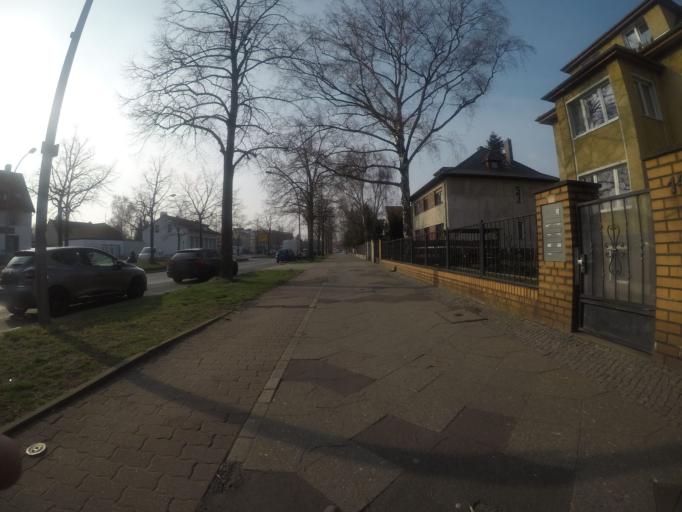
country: DE
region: Berlin
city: Gropiusstadt
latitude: 52.4335
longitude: 13.4714
